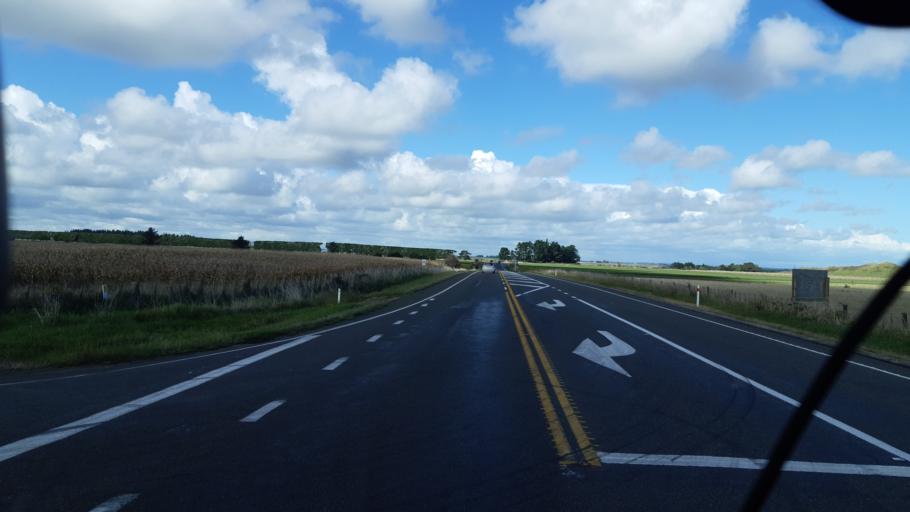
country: NZ
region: Manawatu-Wanganui
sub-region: Wanganui District
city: Wanganui
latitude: -39.9896
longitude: 175.1615
